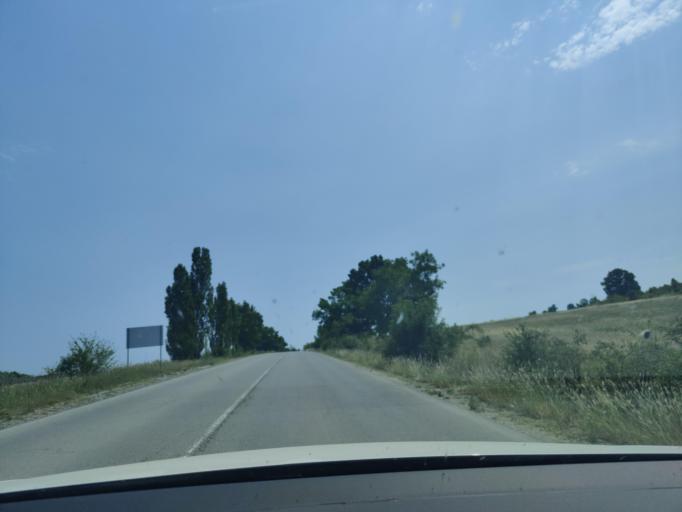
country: BG
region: Montana
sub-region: Obshtina Montana
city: Montana
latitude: 43.4822
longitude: 23.0867
